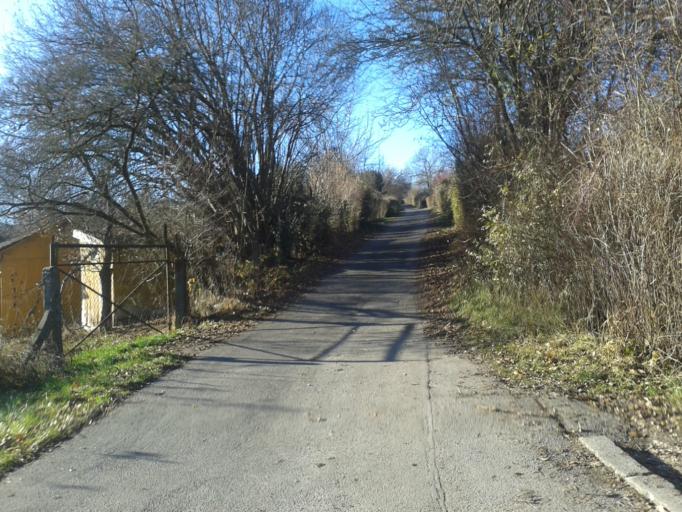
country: DE
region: Baden-Wuerttemberg
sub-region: Tuebingen Region
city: Ulm
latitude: 48.4157
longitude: 9.9689
